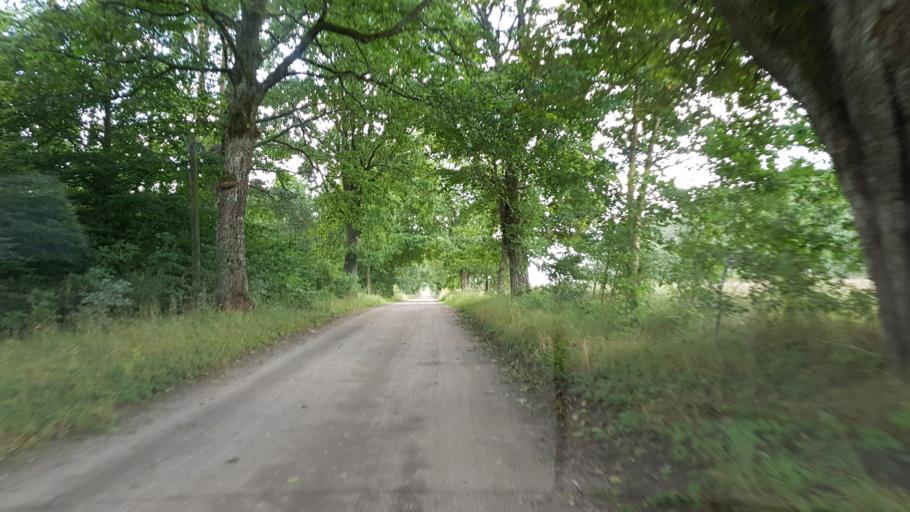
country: PL
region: West Pomeranian Voivodeship
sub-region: Powiat bialogardzki
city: Tychowo
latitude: 54.0010
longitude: 16.3143
